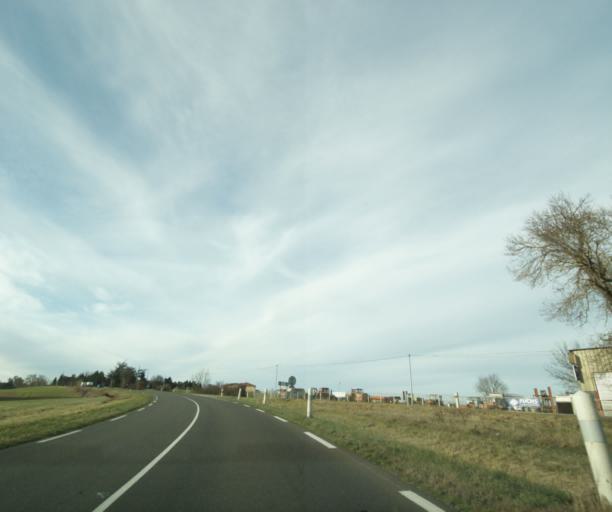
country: FR
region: Midi-Pyrenees
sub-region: Departement du Gers
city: Gimont
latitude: 43.6329
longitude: 0.8569
